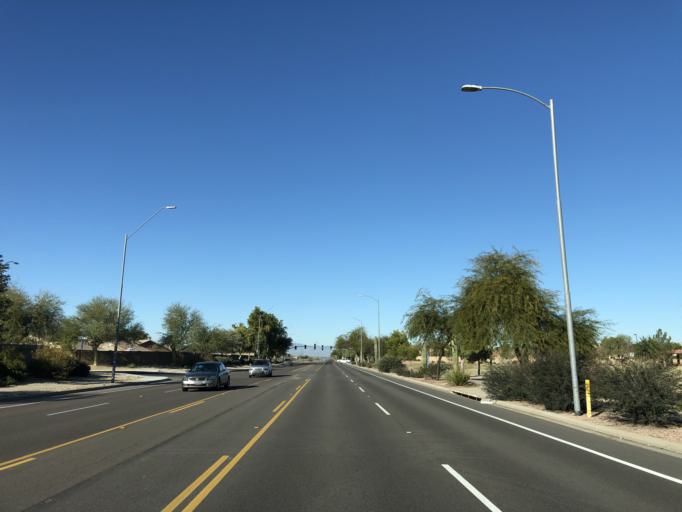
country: US
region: Arizona
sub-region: Maricopa County
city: Sun City West
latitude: 33.6869
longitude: -112.2897
